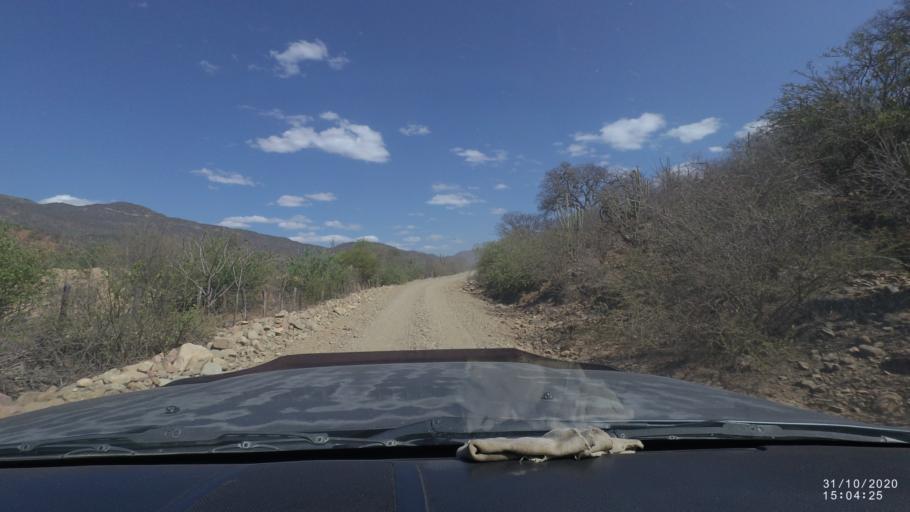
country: BO
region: Cochabamba
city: Aiquile
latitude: -18.2825
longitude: -64.8035
